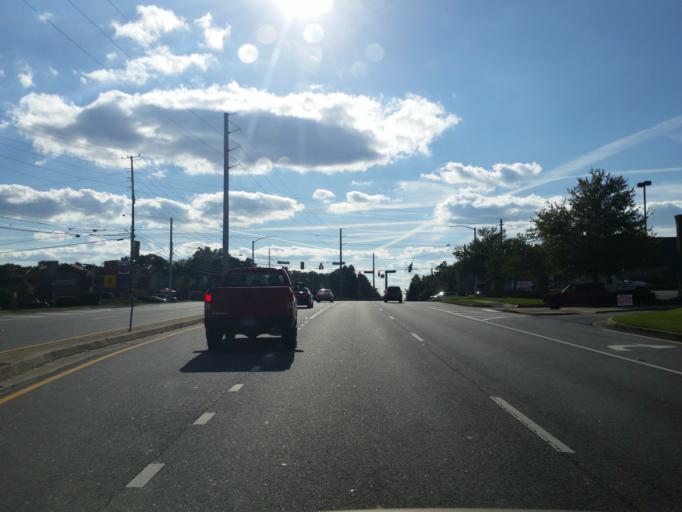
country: US
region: Georgia
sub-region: Cobb County
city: Powder Springs
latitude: 33.9410
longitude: -84.7017
